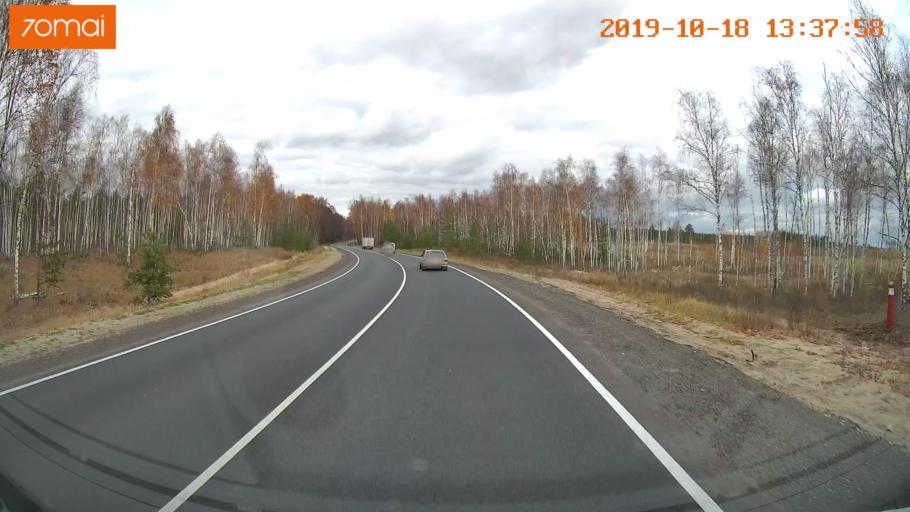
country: RU
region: Rjazan
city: Solotcha
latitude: 54.8847
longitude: 40.0006
